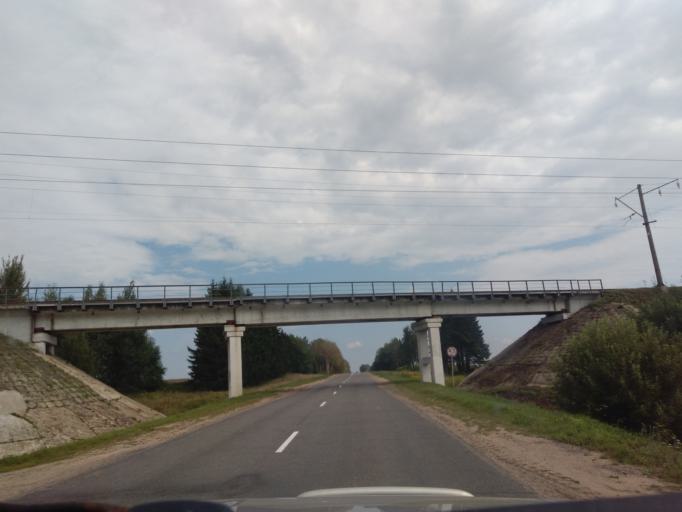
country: BY
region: Minsk
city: Khatsyezhyna
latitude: 53.9129
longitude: 27.3228
